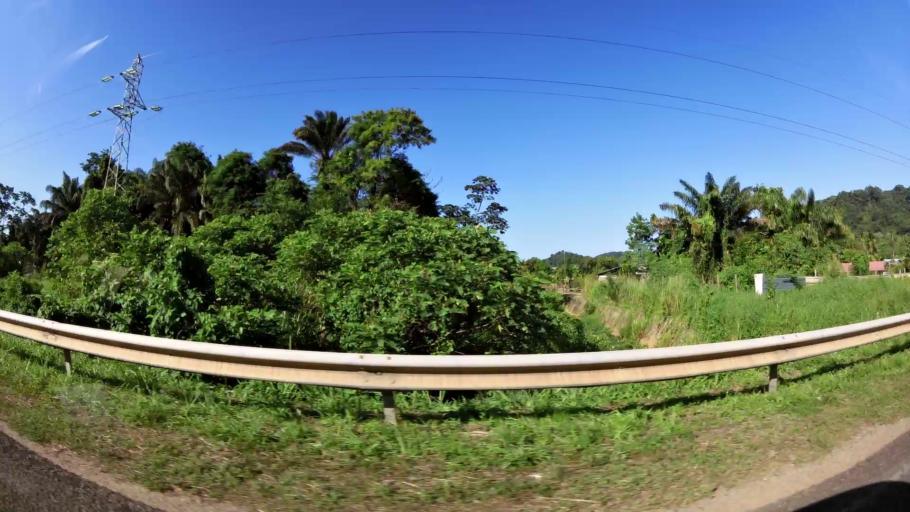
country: GF
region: Guyane
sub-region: Guyane
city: Remire-Montjoly
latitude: 4.8823
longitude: -52.2812
